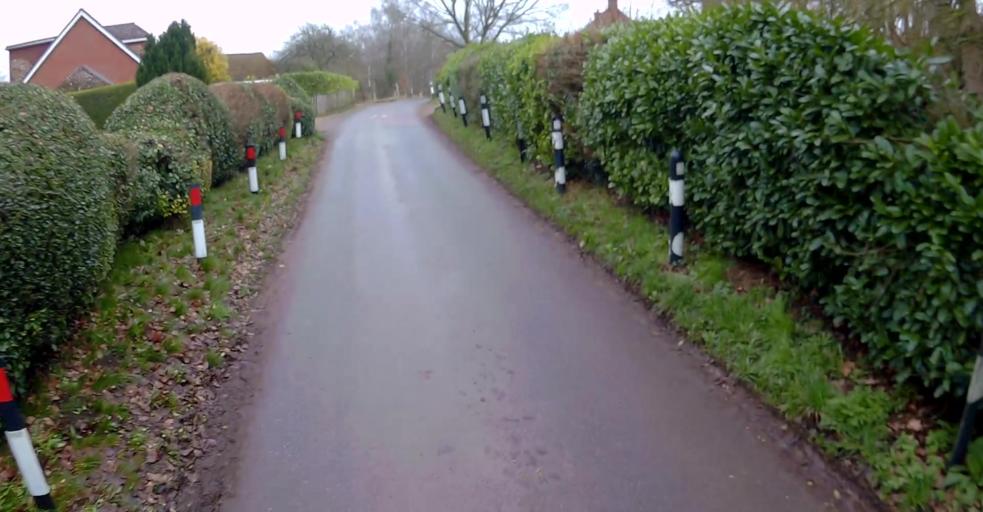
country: GB
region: England
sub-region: Hampshire
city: Eversley
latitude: 51.3291
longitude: -0.9322
